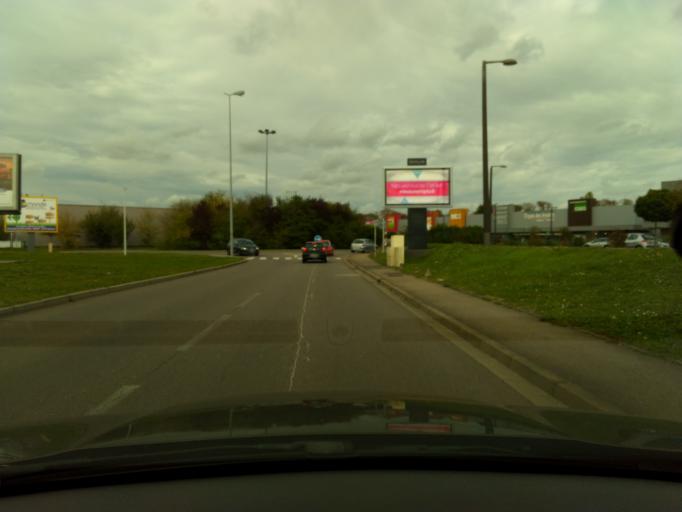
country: FR
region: Lorraine
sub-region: Departement de la Moselle
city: Augny
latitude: 49.0791
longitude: 6.1118
